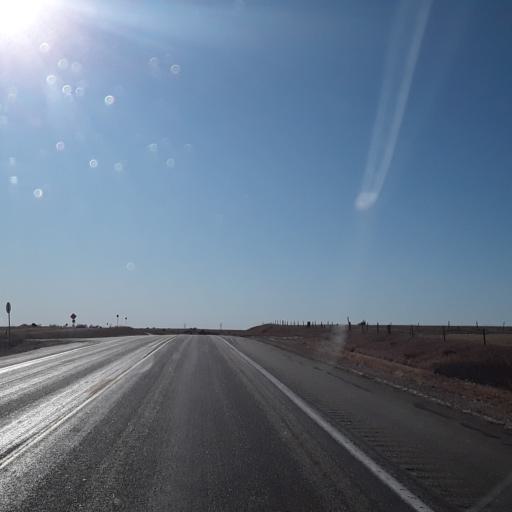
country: US
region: Nebraska
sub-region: Frontier County
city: Stockville
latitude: 40.5484
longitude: -100.6413
